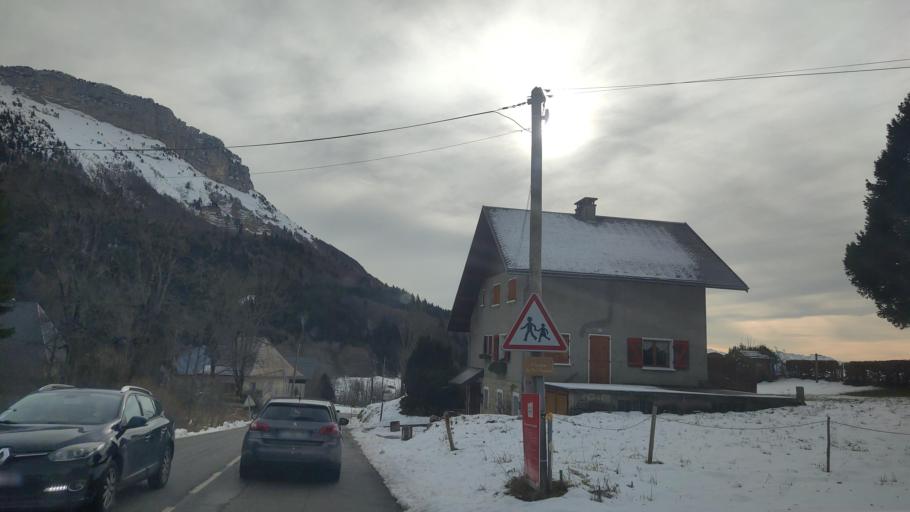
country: FR
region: Rhone-Alpes
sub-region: Departement de la Savoie
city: Mery
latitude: 45.6456
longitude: 6.0143
